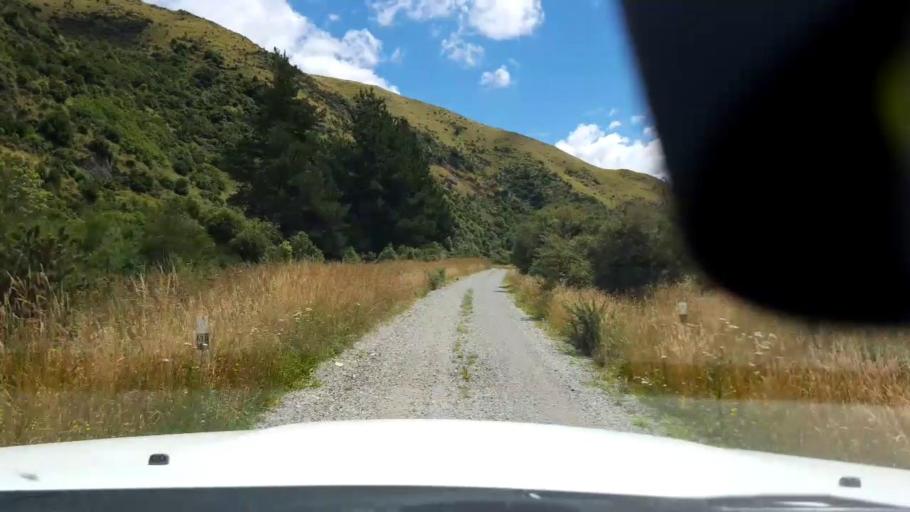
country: NZ
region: Canterbury
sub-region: Timaru District
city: Pleasant Point
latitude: -43.9326
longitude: 171.1954
